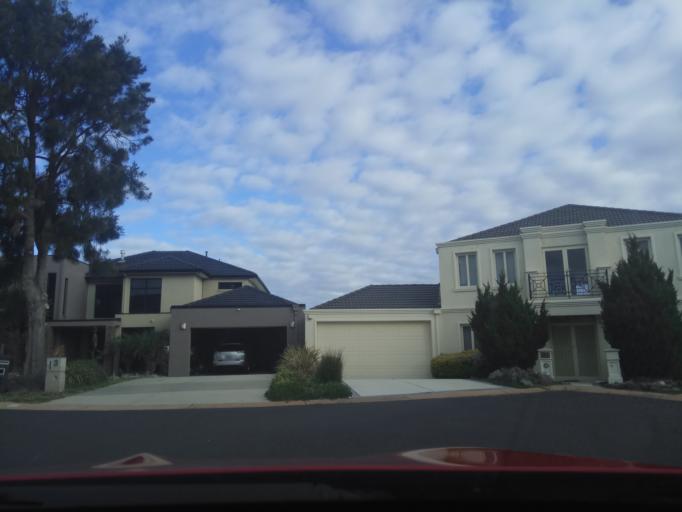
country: AU
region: Victoria
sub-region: Wyndham
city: Point Cook
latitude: -37.9012
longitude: 144.7661
